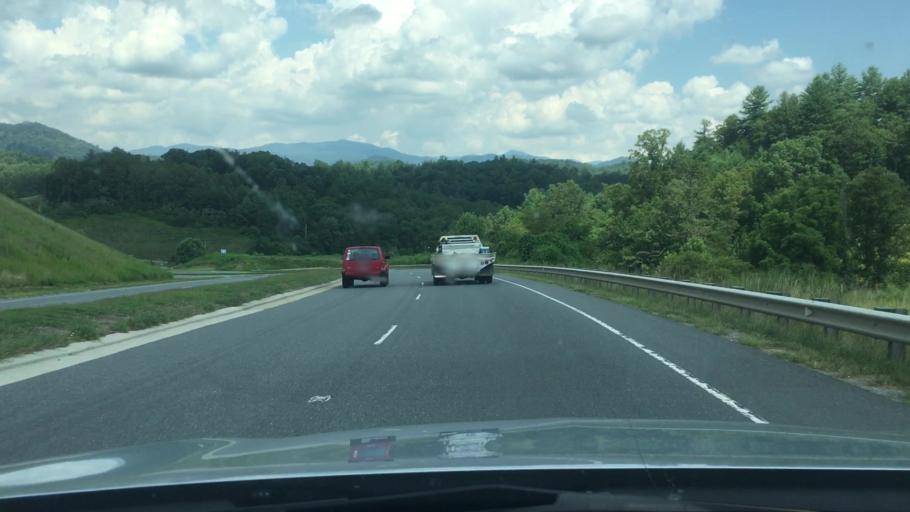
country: US
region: North Carolina
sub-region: Madison County
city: Mars Hill
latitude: 35.8387
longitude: -82.5135
